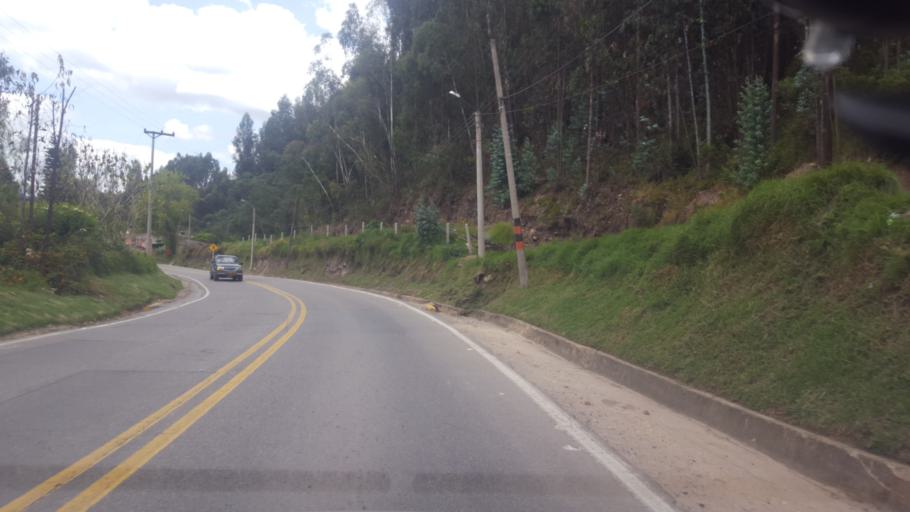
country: CO
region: Boyaca
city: Duitama
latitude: 5.8408
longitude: -73.0155
